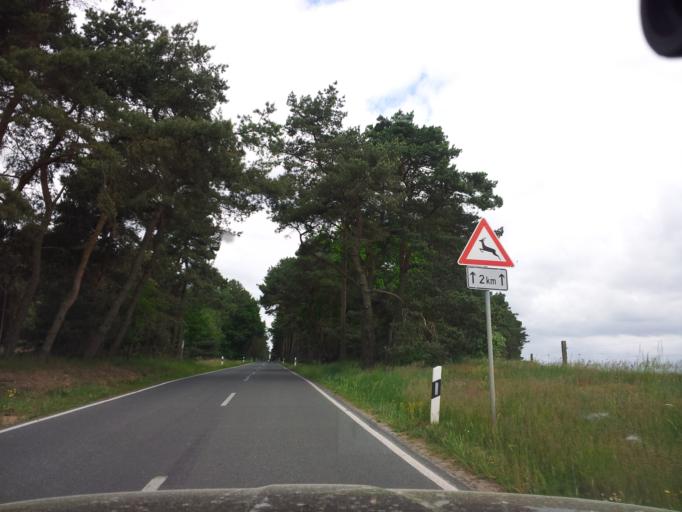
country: DE
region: Brandenburg
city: Treuenbrietzen
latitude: 52.0792
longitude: 12.8053
